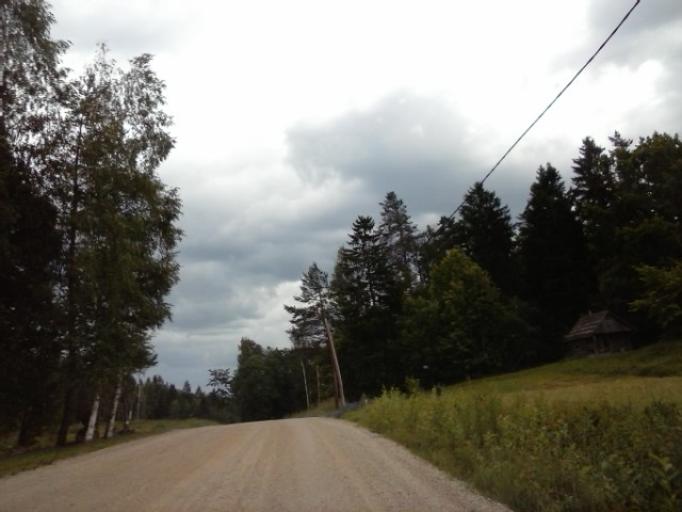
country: EE
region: Vorumaa
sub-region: Voru linn
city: Voru
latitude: 57.7441
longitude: 27.0869
